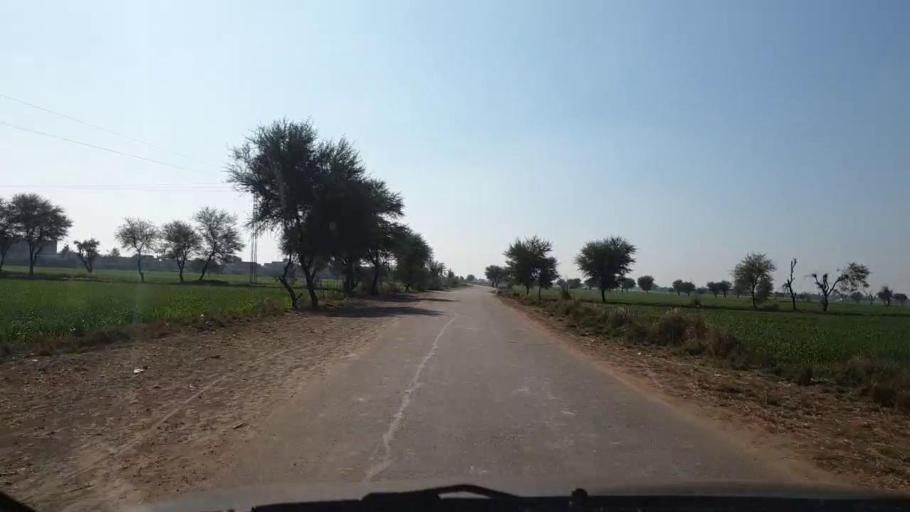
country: PK
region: Sindh
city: Sinjhoro
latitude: 25.9604
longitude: 68.7454
